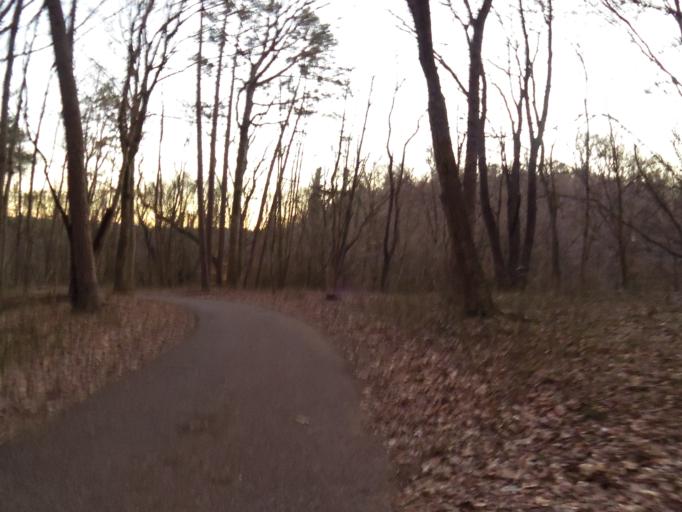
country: US
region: Tennessee
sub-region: Knox County
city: Knoxville
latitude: 35.9548
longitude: -83.8665
